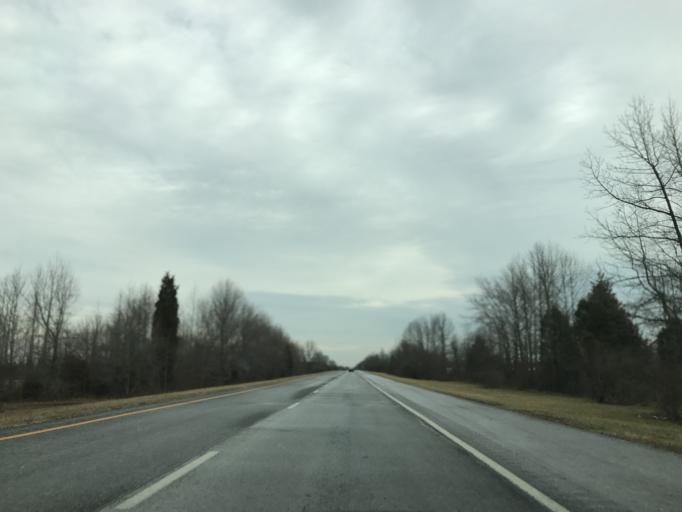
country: US
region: New Jersey
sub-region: Salem County
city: Penns Grove
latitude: 39.7221
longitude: -75.4233
